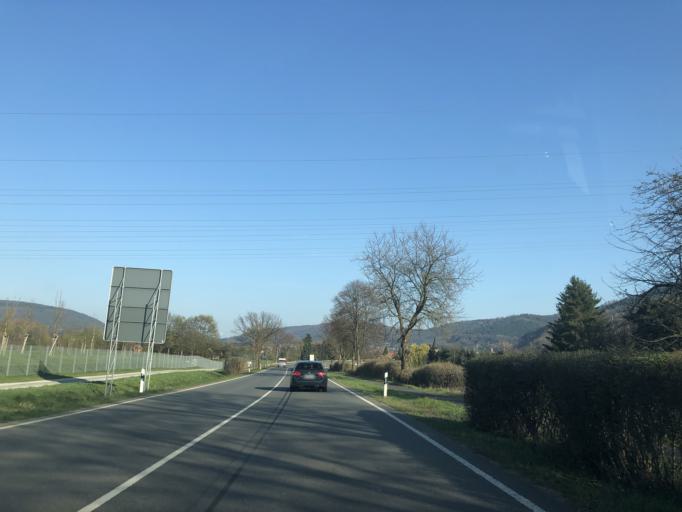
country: DE
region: Bavaria
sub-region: Regierungsbezirk Unterfranken
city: Kleinheubach
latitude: 49.7102
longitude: 9.2217
